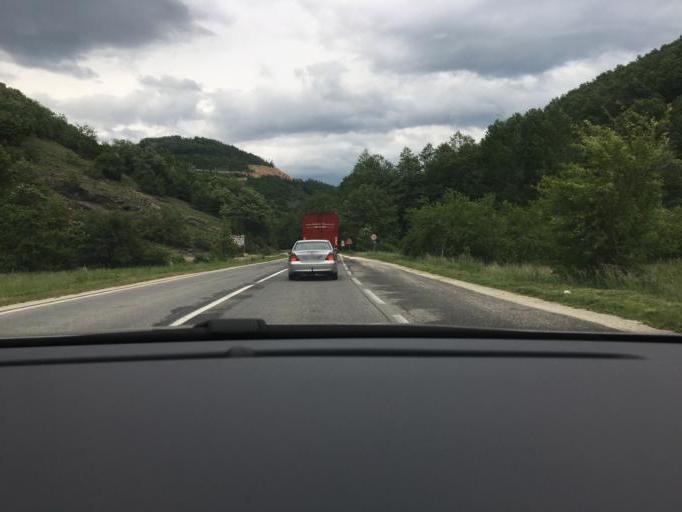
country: MK
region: Drugovo
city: Drugovo
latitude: 41.4809
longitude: 20.8912
